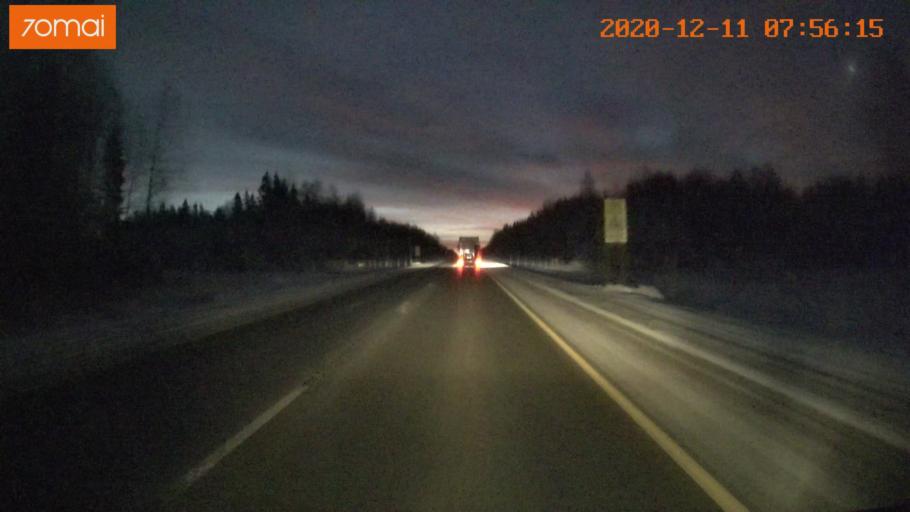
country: RU
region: Vologda
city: Chebsara
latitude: 59.1543
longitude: 38.8219
